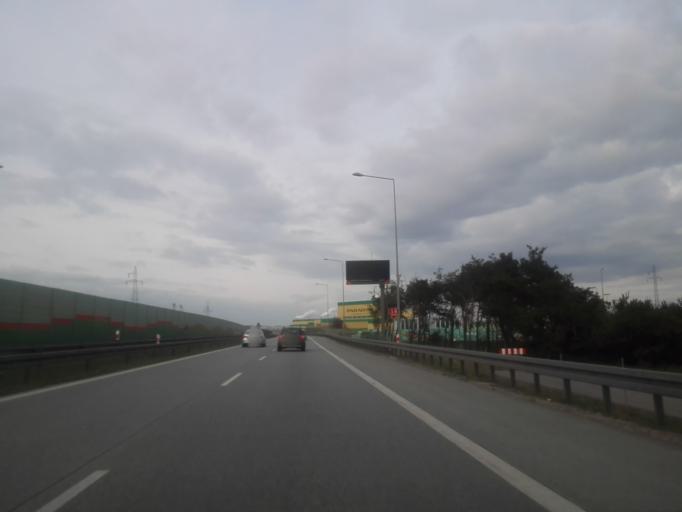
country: PL
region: Lodz Voivodeship
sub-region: Powiat tomaszowski
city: Tomaszow Mazowiecki
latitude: 51.5509
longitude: 19.9927
